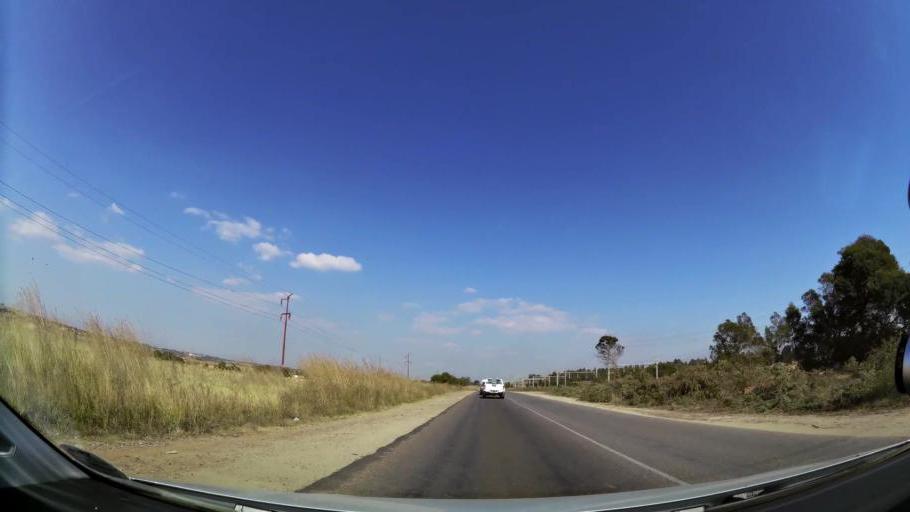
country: ZA
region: Gauteng
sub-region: Ekurhuleni Metropolitan Municipality
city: Tembisa
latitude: -26.0465
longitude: 28.2535
